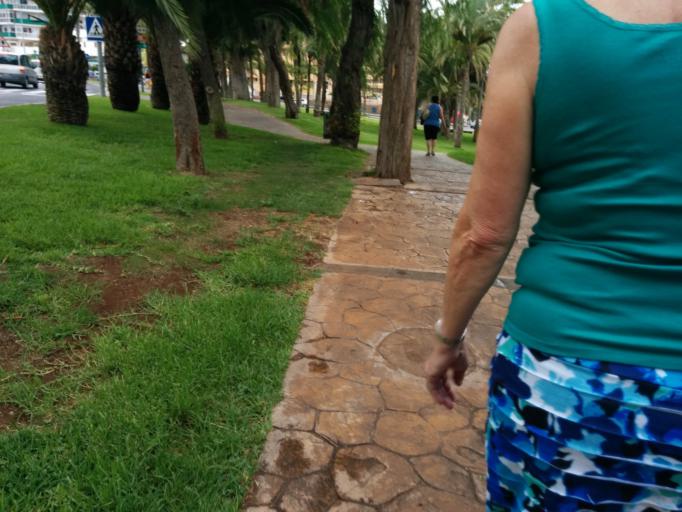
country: ES
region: Canary Islands
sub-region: Provincia de Santa Cruz de Tenerife
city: Playa de las Americas
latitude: 28.0689
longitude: -16.7277
